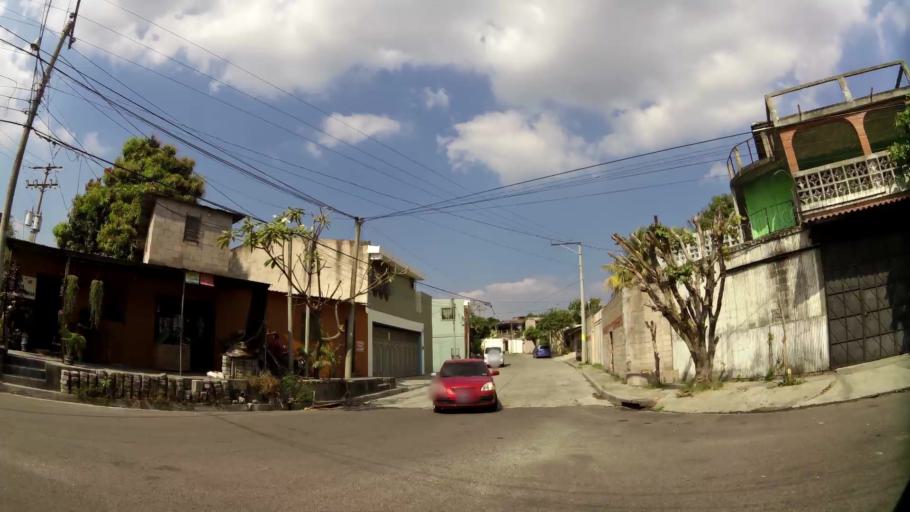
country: SV
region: San Salvador
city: Delgado
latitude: 13.7157
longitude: -89.1711
